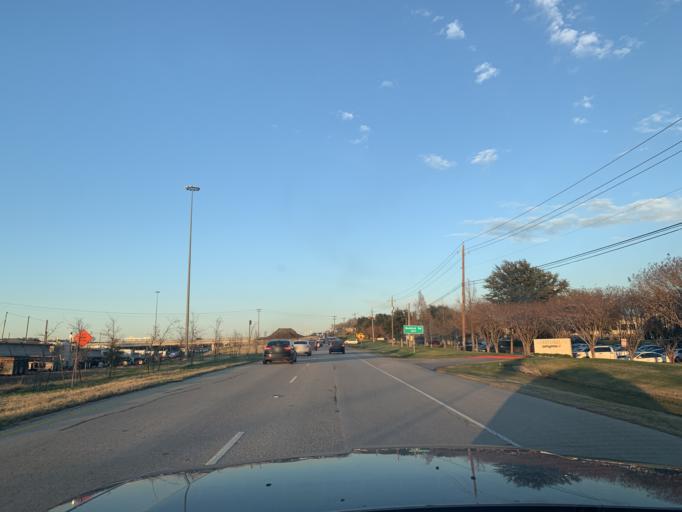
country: US
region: Texas
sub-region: Tarrant County
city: Bedford
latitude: 32.8419
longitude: -97.1169
